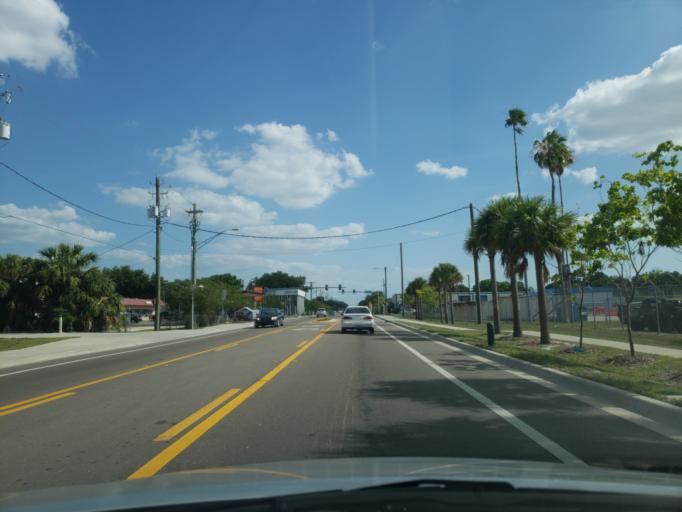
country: US
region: Florida
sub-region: Hillsborough County
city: Egypt Lake-Leto
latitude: 27.9902
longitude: -82.5135
